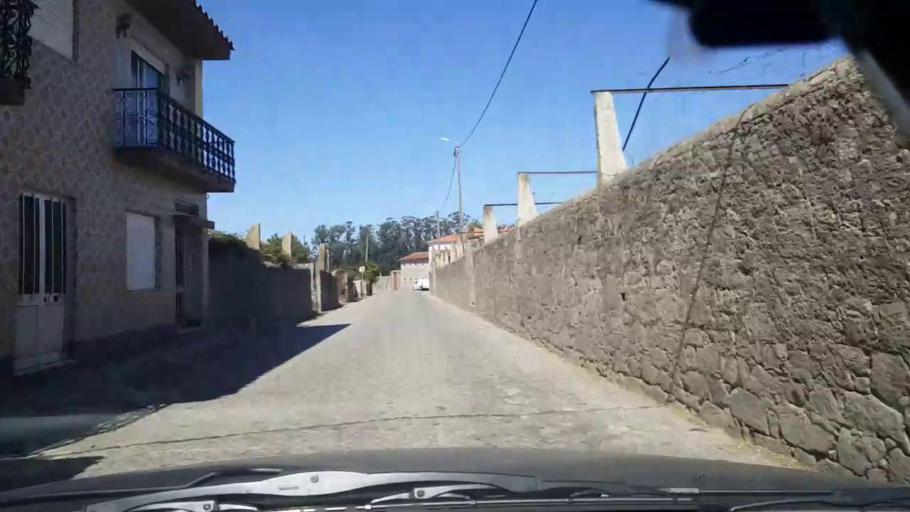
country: PT
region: Porto
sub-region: Vila do Conde
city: Arvore
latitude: 41.3258
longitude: -8.7052
